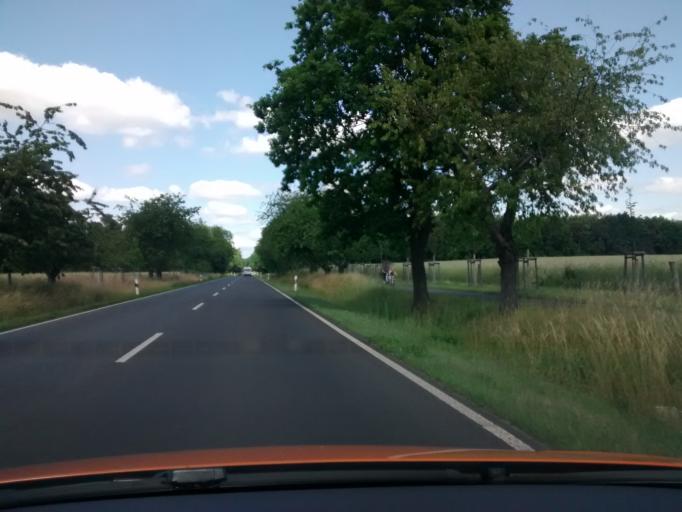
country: DE
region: Berlin
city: Kladow
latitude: 52.4888
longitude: 13.1167
